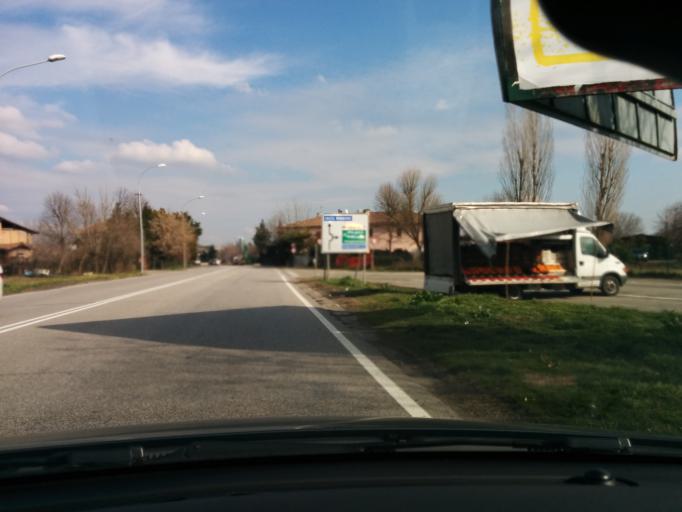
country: IT
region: Emilia-Romagna
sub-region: Provincia di Bologna
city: Trebbo
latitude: 44.5325
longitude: 11.3370
